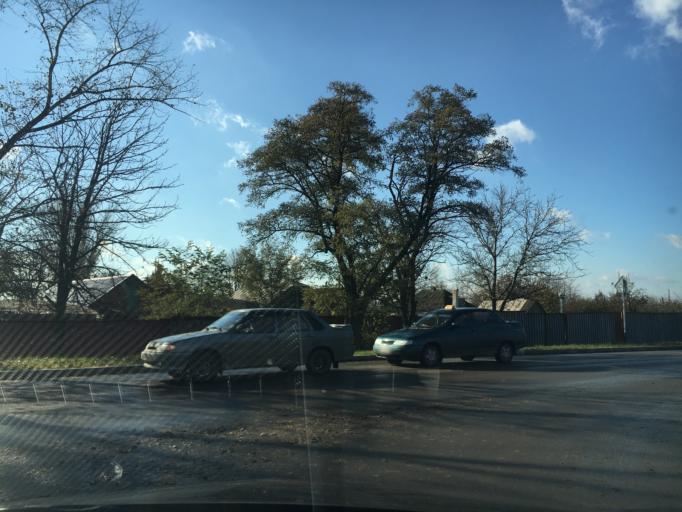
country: RU
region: Rostov
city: Matveyev Kurgan
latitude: 47.5668
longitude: 38.8716
